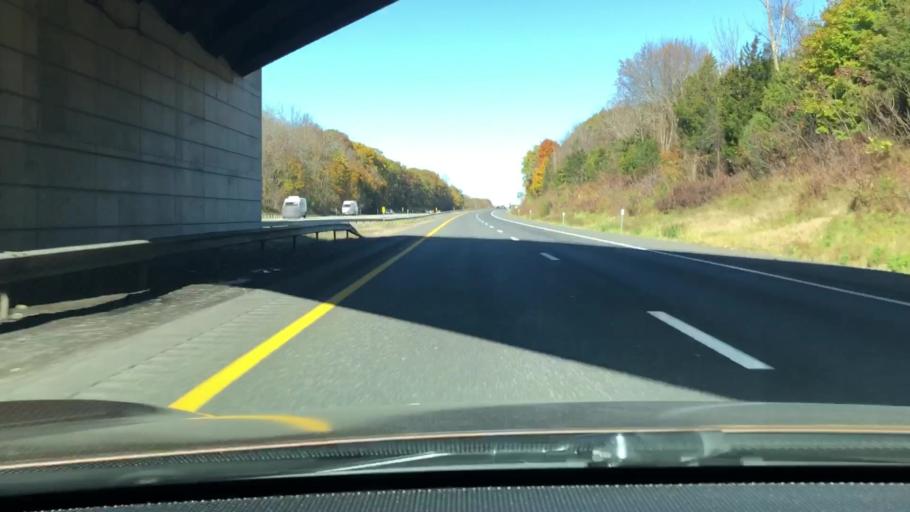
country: US
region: New York
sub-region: Orange County
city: Orange Lake
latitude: 41.5632
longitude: -74.0826
